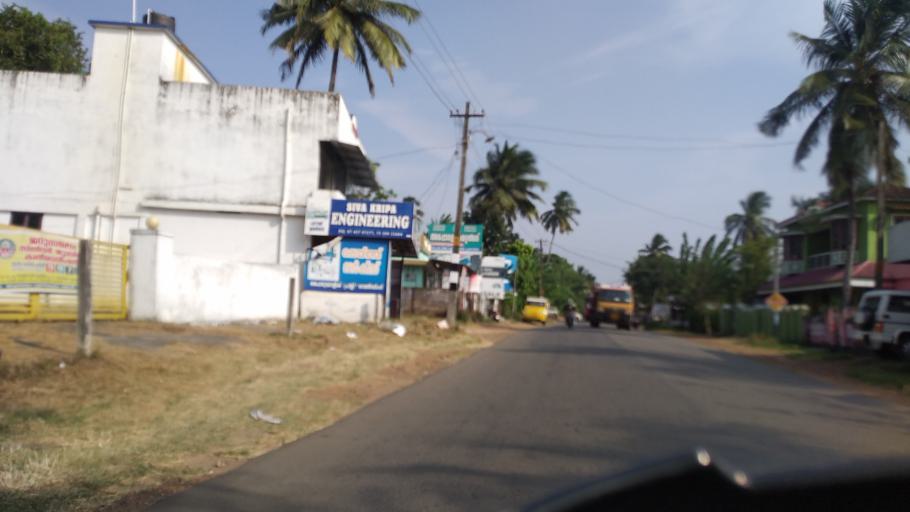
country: IN
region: Kerala
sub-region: Thrissur District
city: Chelakara
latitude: 10.6011
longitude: 76.4934
